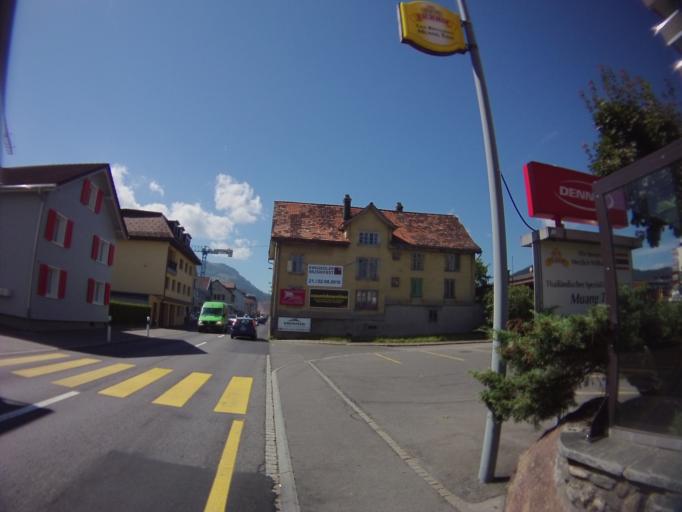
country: CH
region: Schwyz
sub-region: Bezirk Einsiedeln
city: Einsiedeln
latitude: 47.1311
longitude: 8.7440
